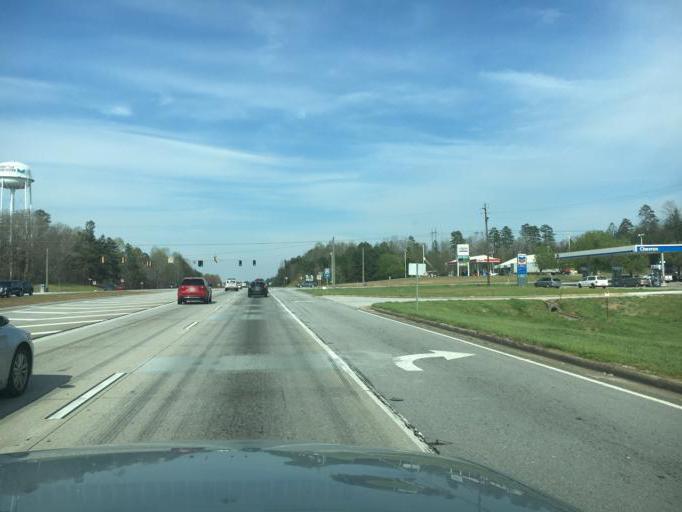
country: US
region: Georgia
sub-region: Hall County
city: Lula
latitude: 34.3942
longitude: -83.6924
